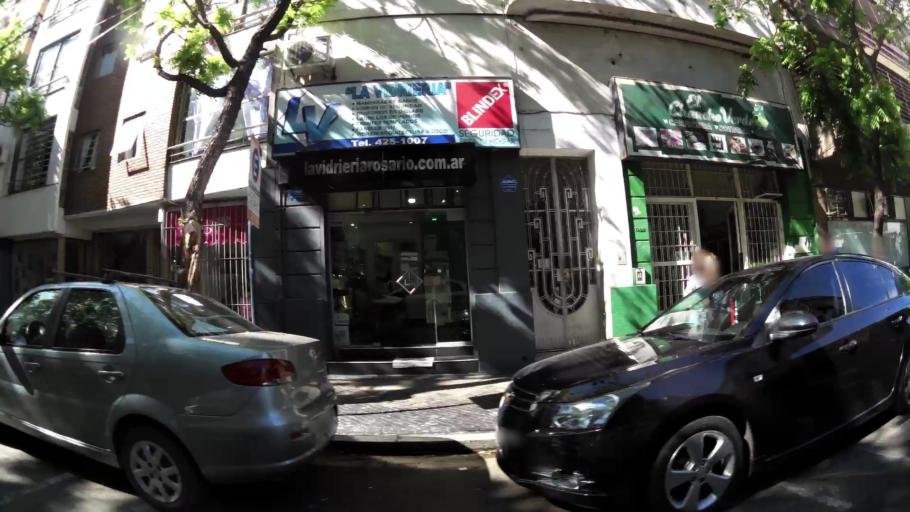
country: AR
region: Santa Fe
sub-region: Departamento de Rosario
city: Rosario
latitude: -32.9499
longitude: -60.6489
